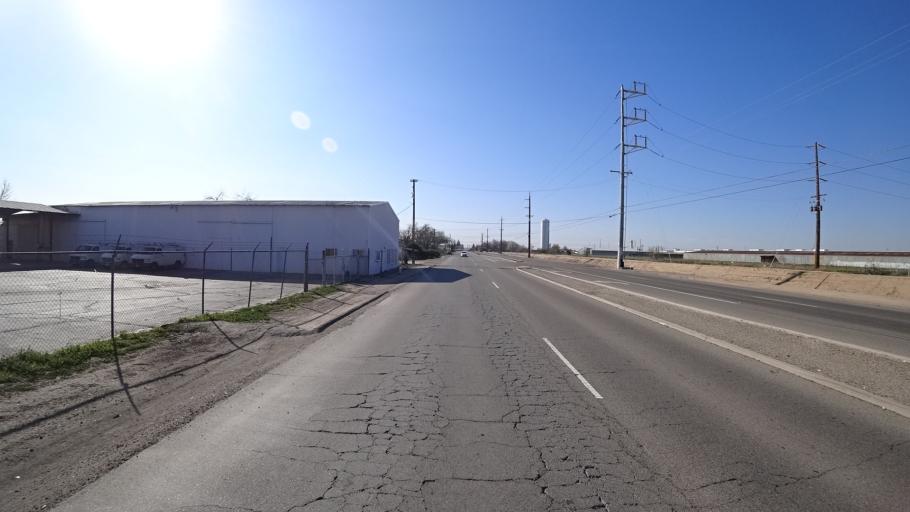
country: US
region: California
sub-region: Fresno County
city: Fresno
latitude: 36.6965
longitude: -119.7364
